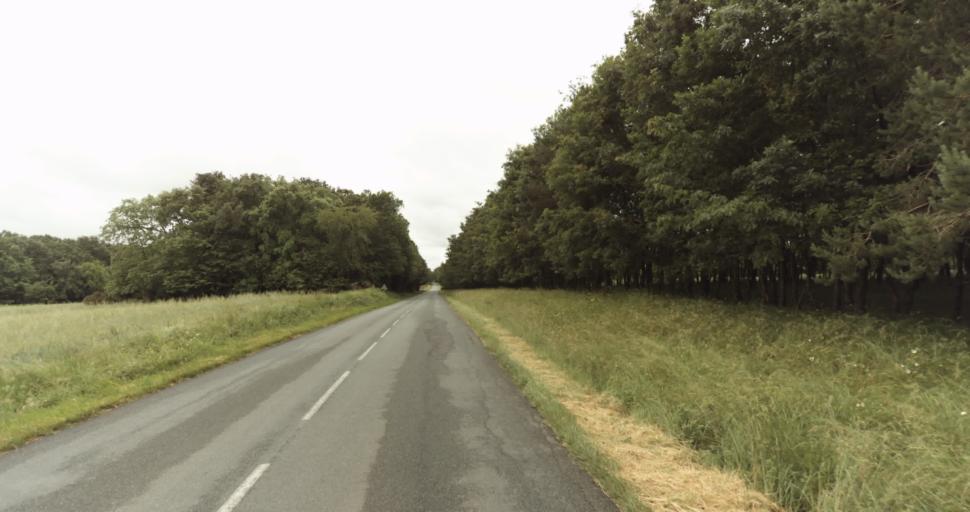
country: FR
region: Aquitaine
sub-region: Departement de la Dordogne
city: Belves
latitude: 44.7012
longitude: 0.9194
